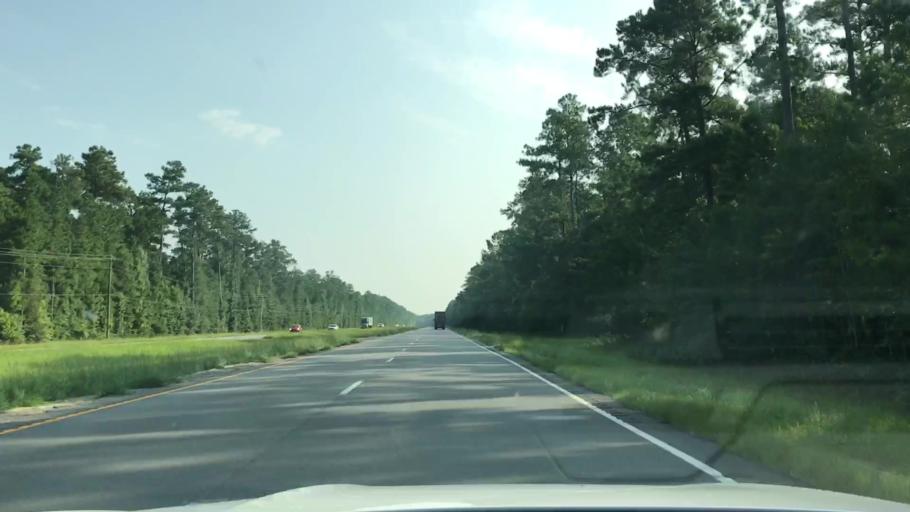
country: US
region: South Carolina
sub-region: Georgetown County
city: Georgetown
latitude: 33.2622
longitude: -79.3646
